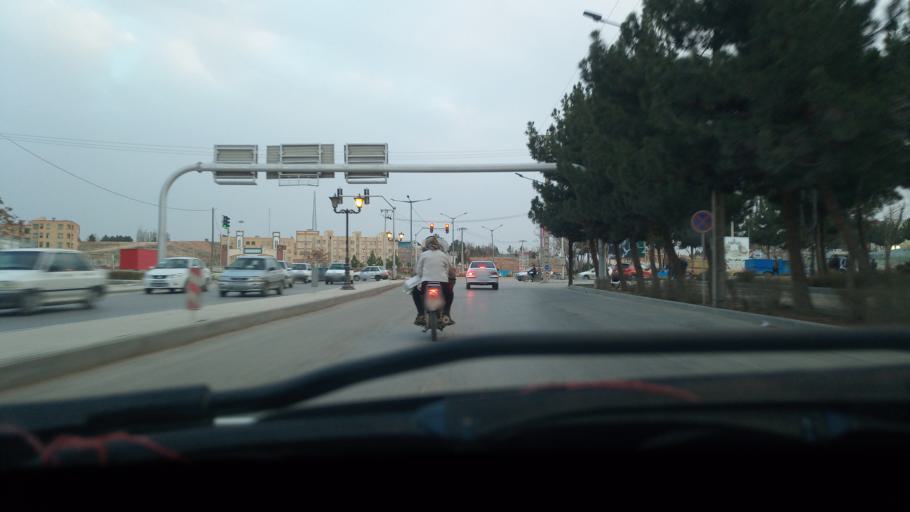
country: IR
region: Khorasan-e Shomali
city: Bojnurd
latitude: 37.4608
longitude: 57.3323
